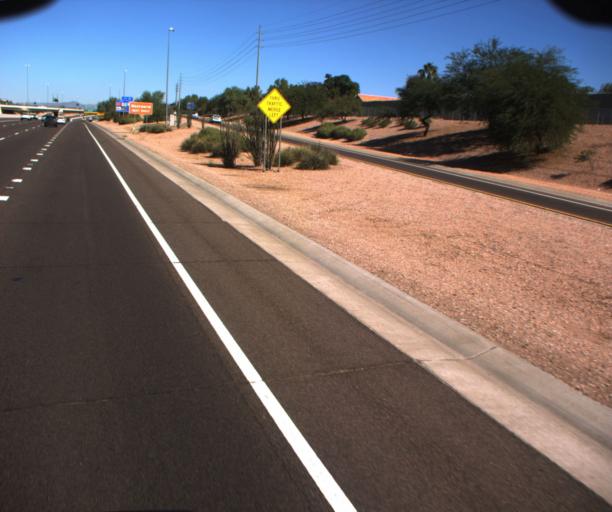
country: US
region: Arizona
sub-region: Maricopa County
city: Paradise Valley
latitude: 33.6142
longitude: -111.8912
